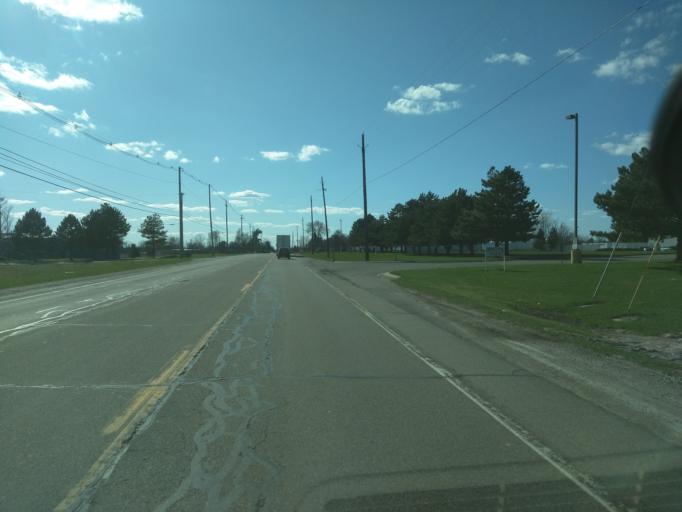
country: US
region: Michigan
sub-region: Eaton County
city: Waverly
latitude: 42.7776
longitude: -84.6321
